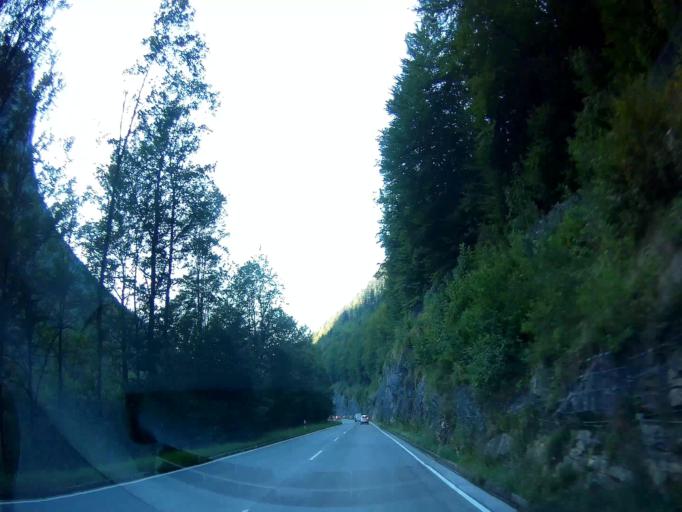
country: DE
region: Bavaria
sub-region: Upper Bavaria
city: Schneizlreuth
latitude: 47.6605
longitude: 12.8465
